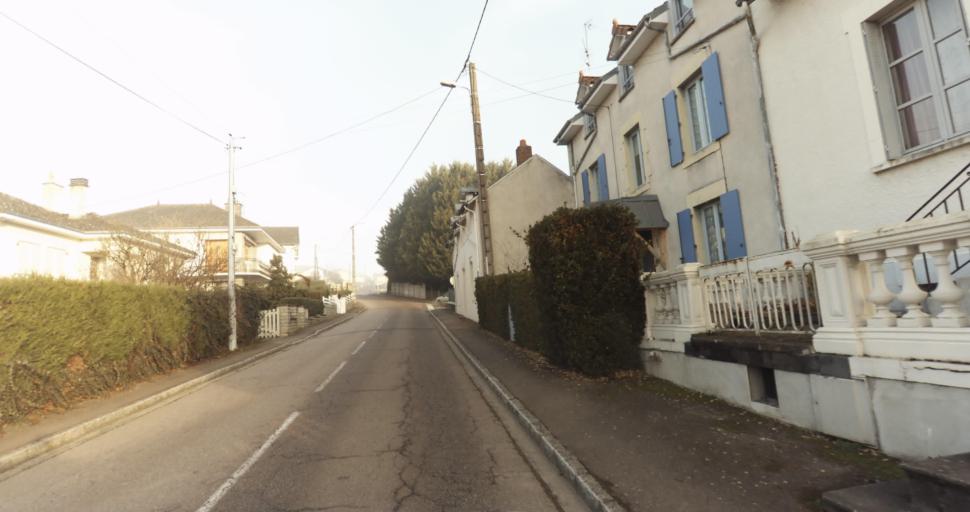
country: FR
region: Limousin
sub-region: Departement de la Haute-Vienne
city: Aixe-sur-Vienne
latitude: 45.7968
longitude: 1.1488
